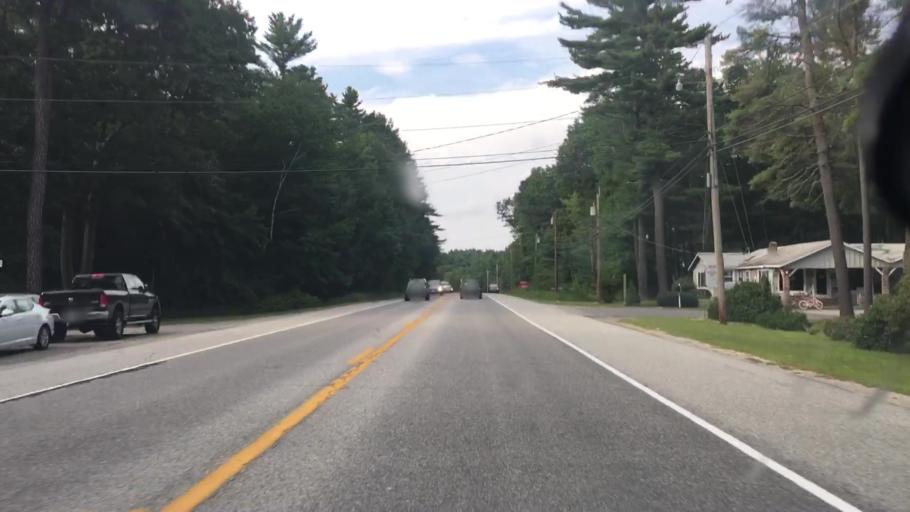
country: US
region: Maine
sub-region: Cumberland County
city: Raymond
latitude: 43.8715
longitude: -70.4648
